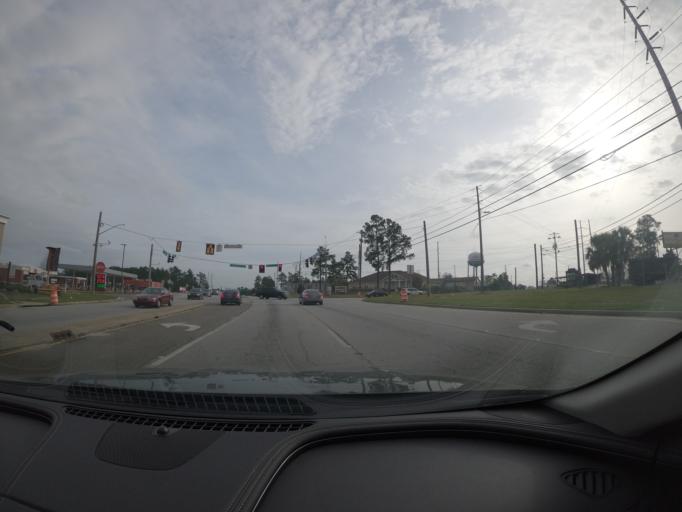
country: US
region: Georgia
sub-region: Columbia County
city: Martinez
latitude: 33.4908
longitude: -82.1100
